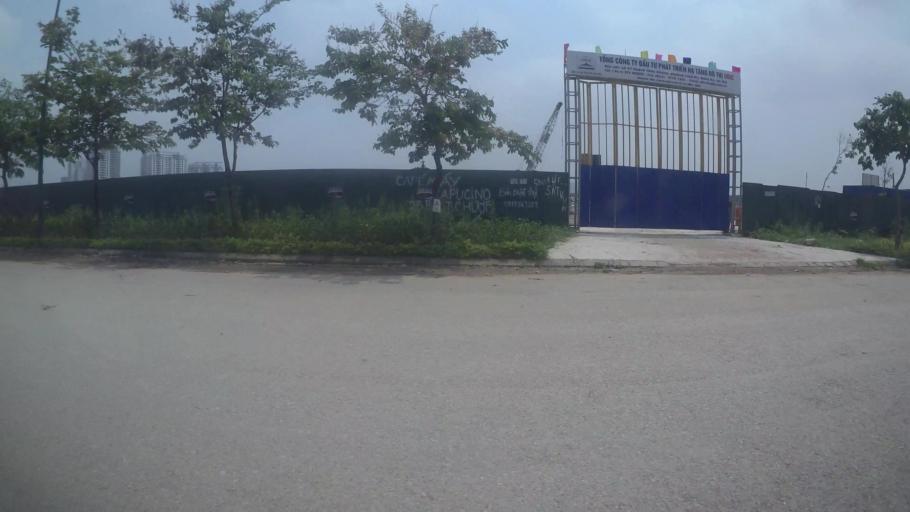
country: VN
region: Ha Noi
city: Tay Ho
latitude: 21.0845
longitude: 105.8087
